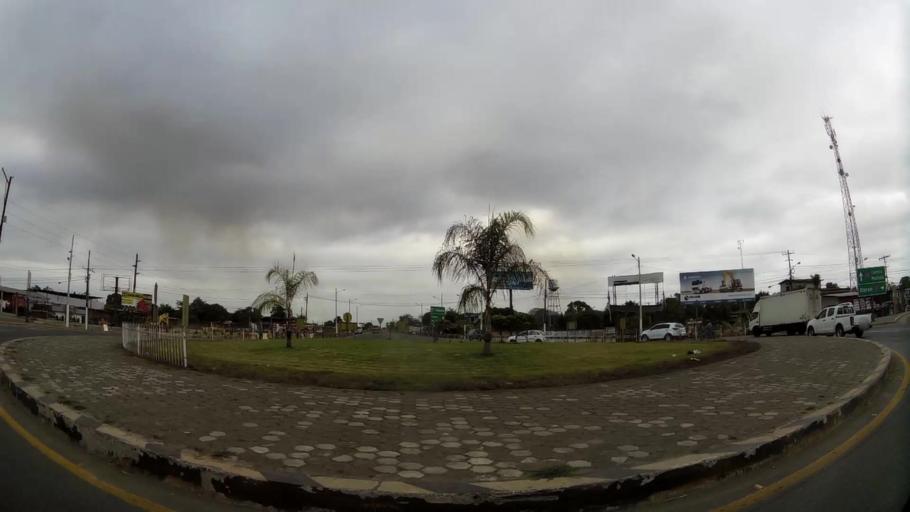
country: EC
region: Guayas
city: Yaguachi Nuevo
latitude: -2.2517
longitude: -79.6357
